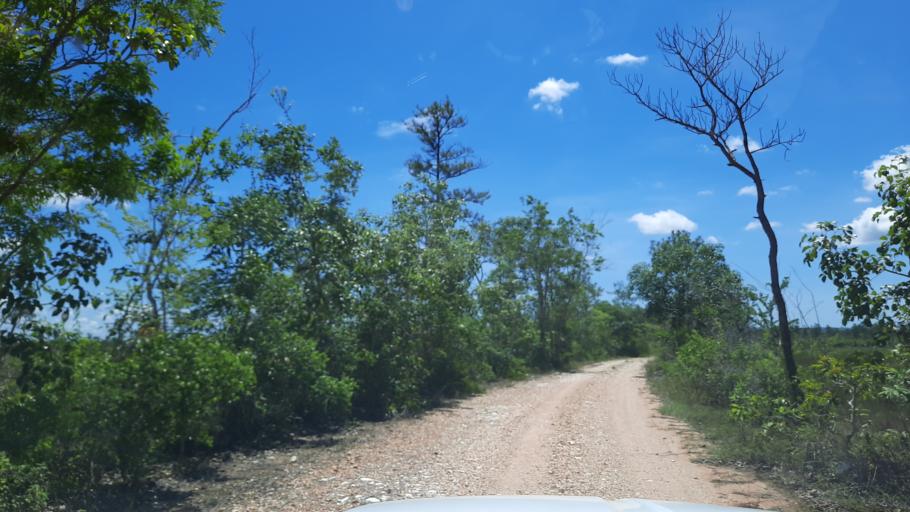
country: BZ
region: Cayo
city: Belmopan
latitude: 17.3545
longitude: -88.5494
